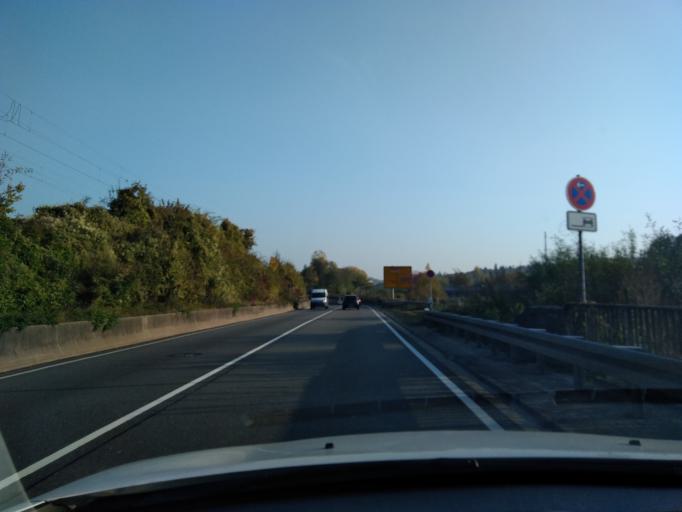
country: DE
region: Saarland
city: Kleinblittersdorf
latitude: 49.1543
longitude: 7.0347
